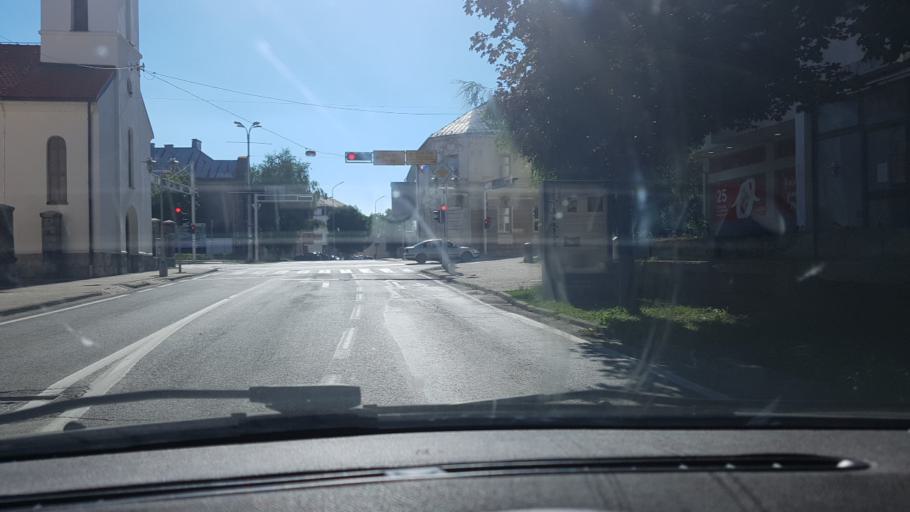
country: HR
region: Licko-Senjska
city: Gospic
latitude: 44.5454
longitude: 15.3735
